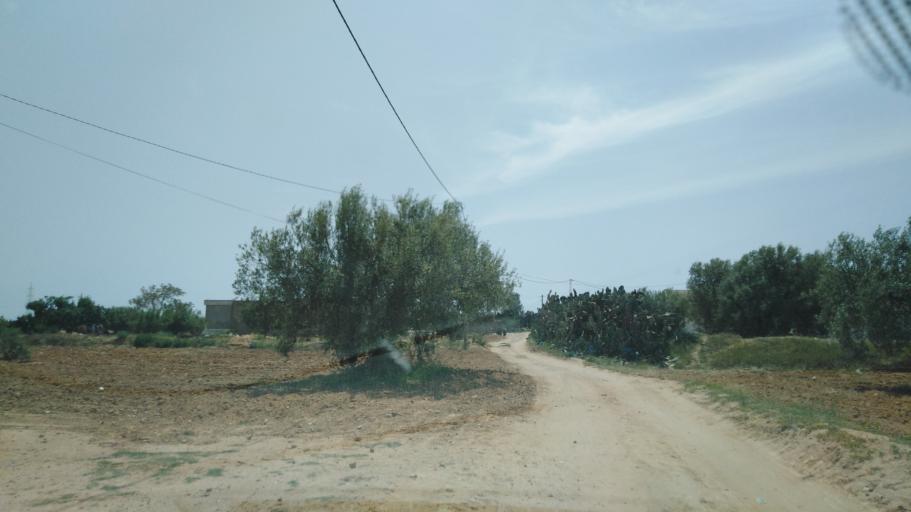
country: TN
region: Safaqis
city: Sfax
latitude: 34.7295
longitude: 10.5554
